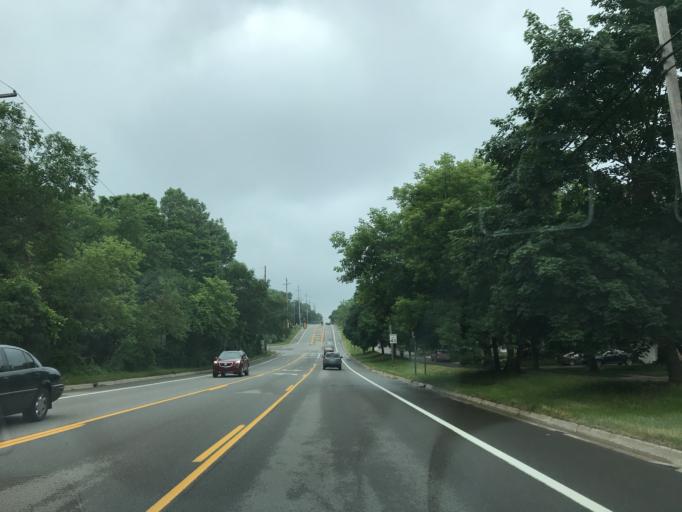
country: US
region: Michigan
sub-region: Washtenaw County
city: Ypsilanti
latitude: 42.2579
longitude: -83.6407
